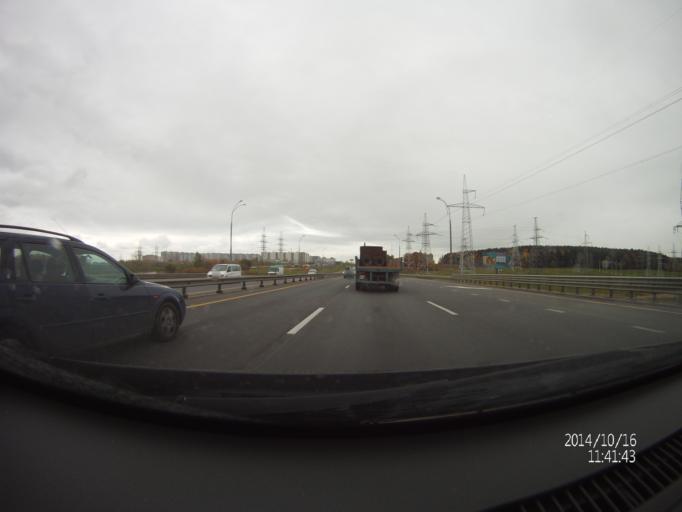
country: BY
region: Minsk
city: Malinovka
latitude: 53.8706
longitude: 27.4222
